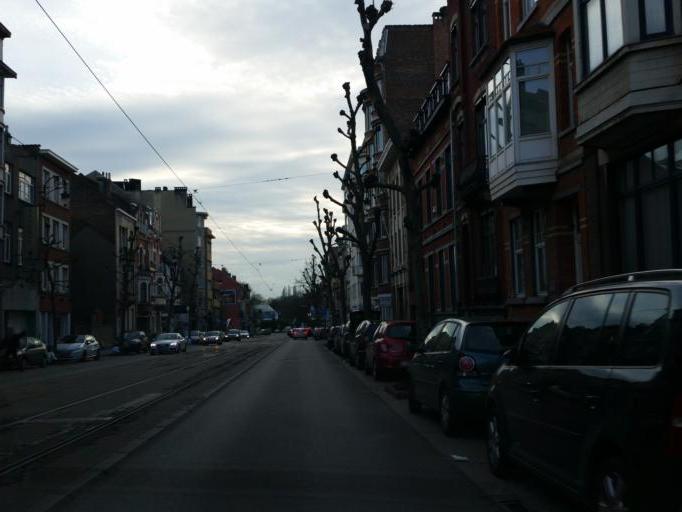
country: BE
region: Flanders
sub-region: Provincie Vlaams-Brabant
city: Drogenbos
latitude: 50.8015
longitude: 4.3392
